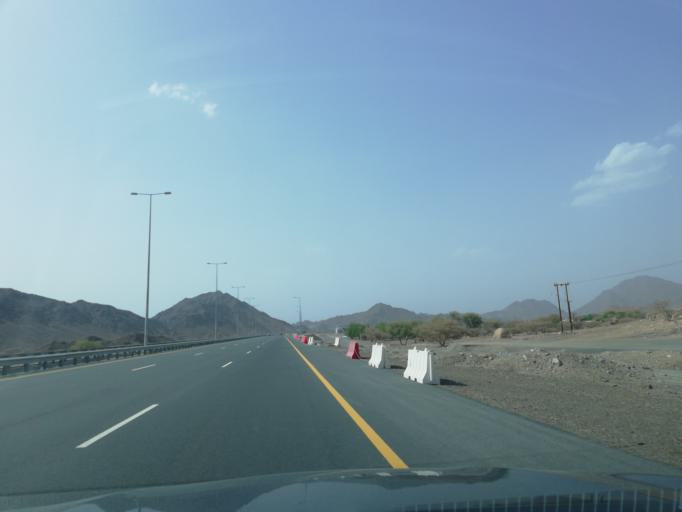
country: OM
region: Ash Sharqiyah
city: Ibra'
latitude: 22.9435
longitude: 58.2484
